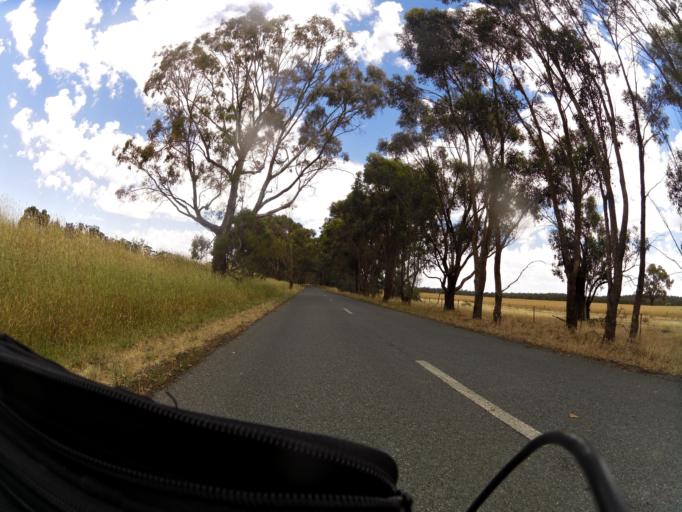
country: AU
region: Victoria
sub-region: Greater Shepparton
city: Shepparton
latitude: -36.6522
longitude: 145.2044
